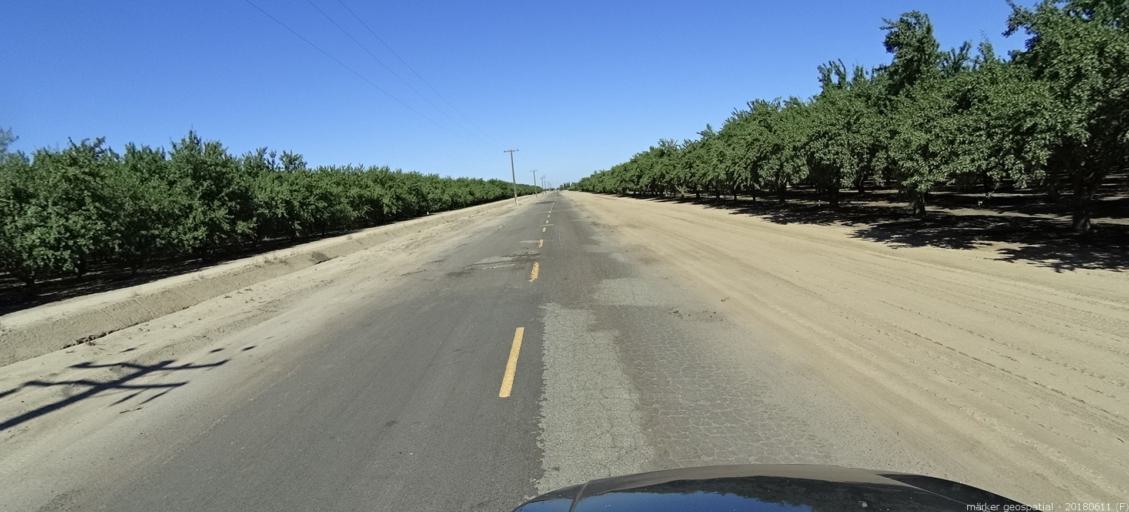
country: US
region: California
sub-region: Madera County
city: Madera
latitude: 36.9456
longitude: -120.1293
